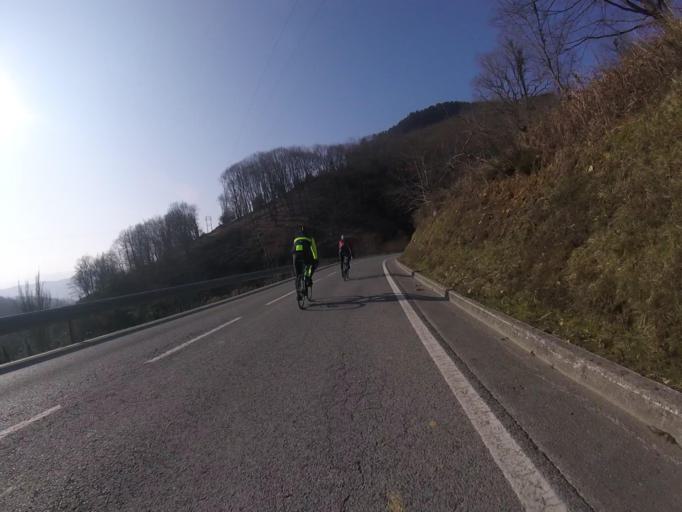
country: ES
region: Navarre
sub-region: Provincia de Navarra
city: Bera
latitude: 43.3066
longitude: -1.6894
